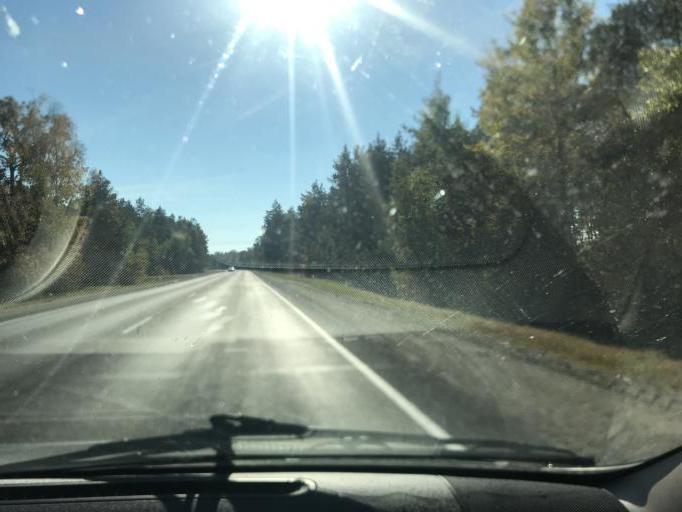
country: BY
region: Brest
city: Mikashevichy
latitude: 52.2566
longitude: 27.4405
